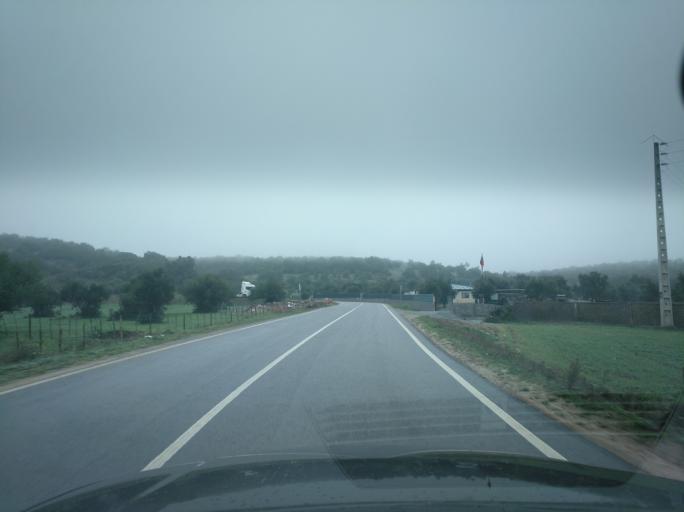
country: PT
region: Portalegre
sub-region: Elvas
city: Elvas
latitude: 38.8974
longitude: -7.1402
